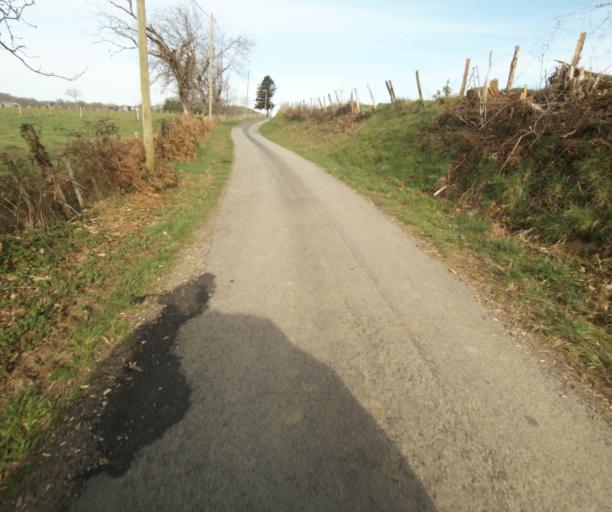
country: FR
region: Limousin
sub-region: Departement de la Correze
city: Chamboulive
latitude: 45.4293
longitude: 1.7433
